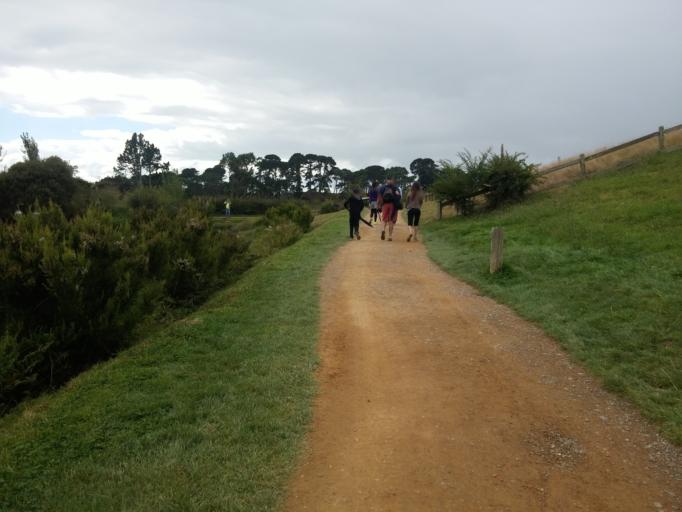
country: NZ
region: Waikato
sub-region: Matamata-Piako District
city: Matamata
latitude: -37.8594
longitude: 175.6814
